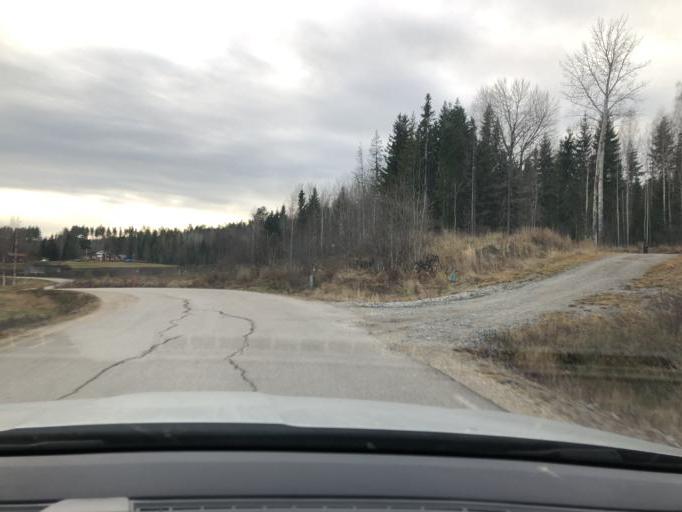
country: SE
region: Gaevleborg
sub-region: Hudiksvalls Kommun
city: Sorforsa
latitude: 61.6624
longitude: 16.9258
